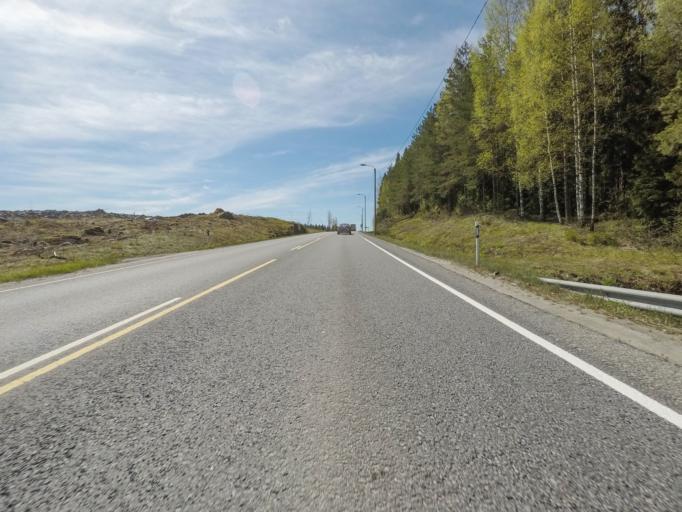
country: FI
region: Pirkanmaa
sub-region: Etelae-Pirkanmaa
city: Urjala
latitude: 61.0657
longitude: 23.5215
